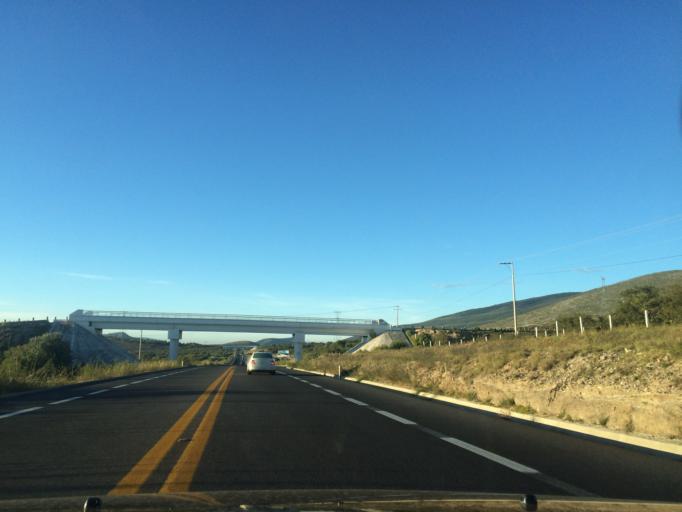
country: MX
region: Puebla
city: Morelos Canada
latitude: 18.7117
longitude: -97.4695
